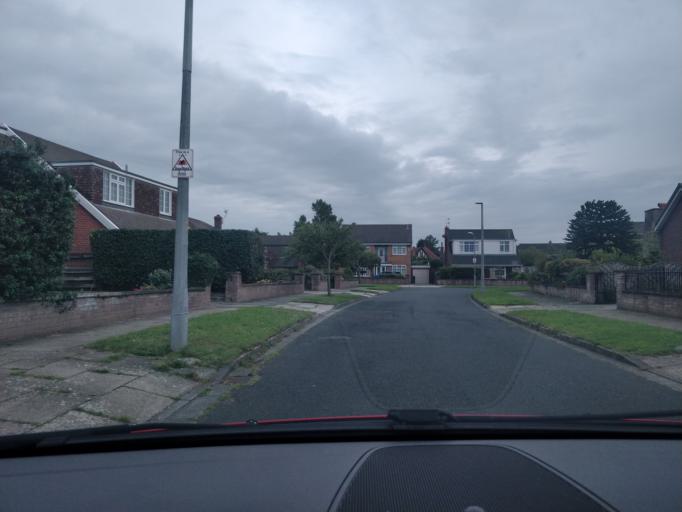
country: GB
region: England
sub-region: Sefton
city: Southport
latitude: 53.6382
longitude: -3.0261
